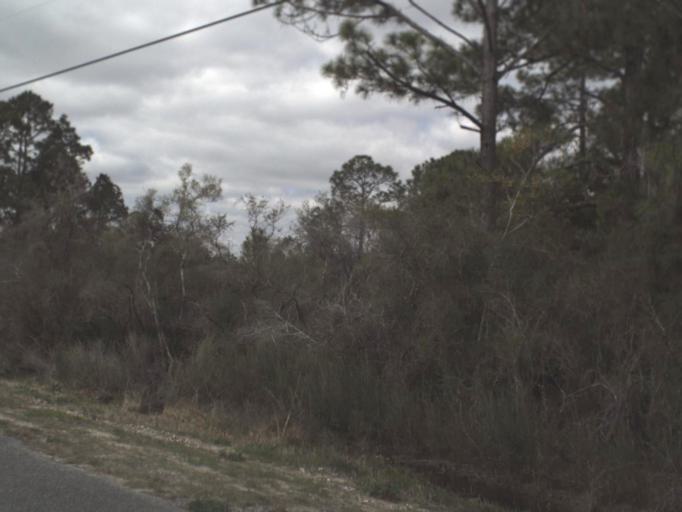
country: US
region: Florida
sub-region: Franklin County
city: Carrabelle
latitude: 29.8245
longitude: -84.7055
